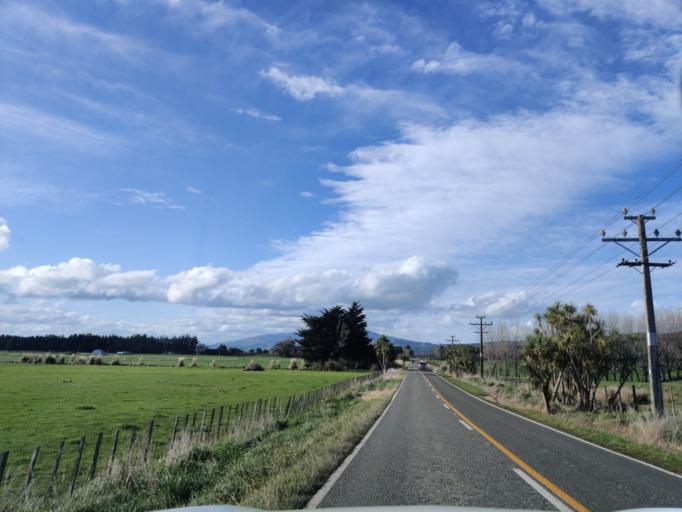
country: NZ
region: Manawatu-Wanganui
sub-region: Palmerston North City
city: Palmerston North
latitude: -40.3432
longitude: 175.7127
